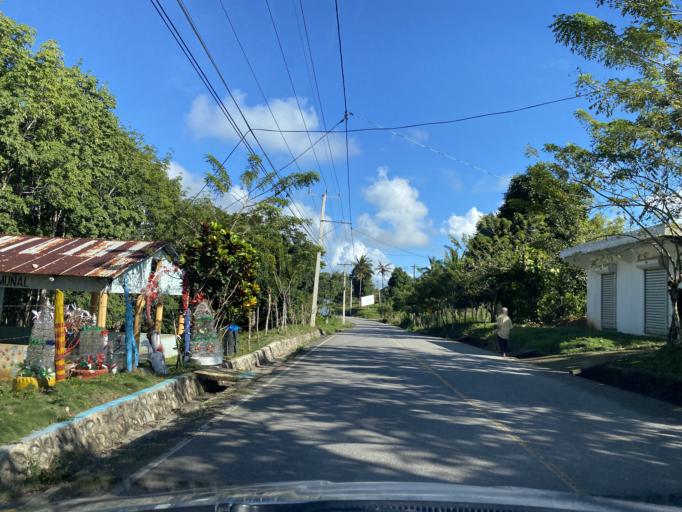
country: DO
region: Samana
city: Sanchez
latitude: 19.2511
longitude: -69.5864
